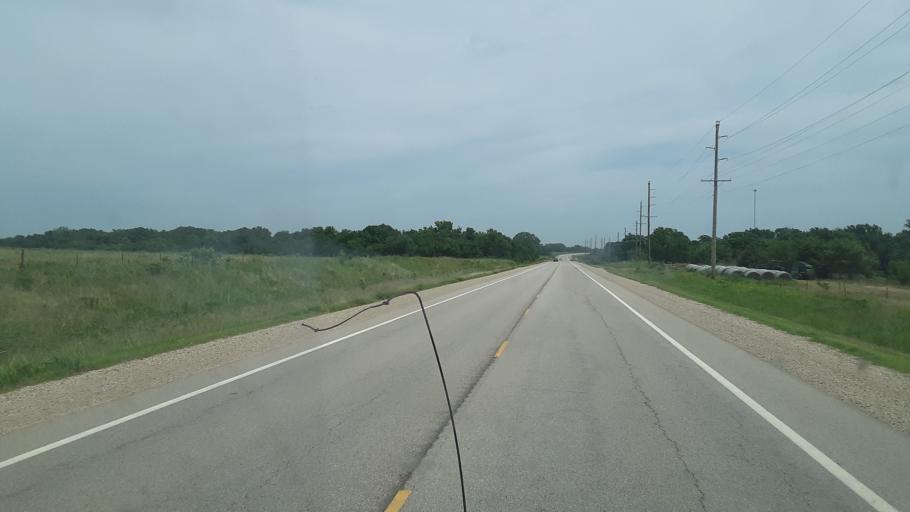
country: US
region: Kansas
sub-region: Greenwood County
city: Eureka
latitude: 37.8342
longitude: -96.1932
